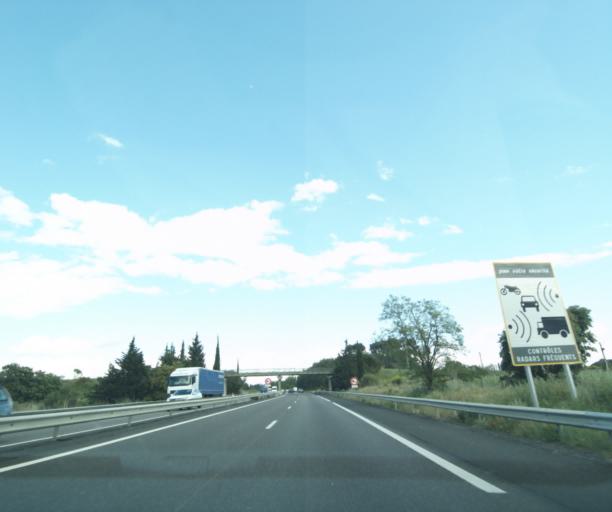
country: FR
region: Languedoc-Roussillon
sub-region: Departement du Gard
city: Garons
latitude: 43.7445
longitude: 4.4409
